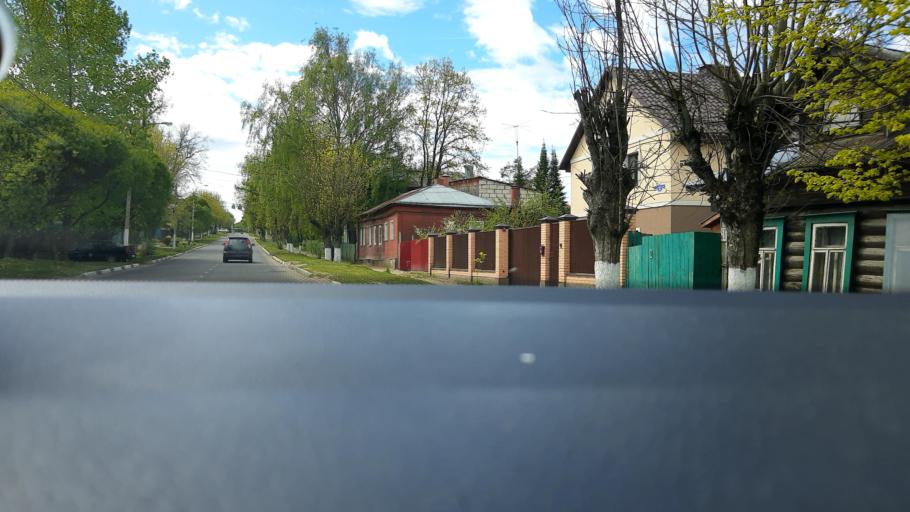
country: RU
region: Moskovskaya
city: Dmitrov
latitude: 56.3453
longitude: 37.5269
